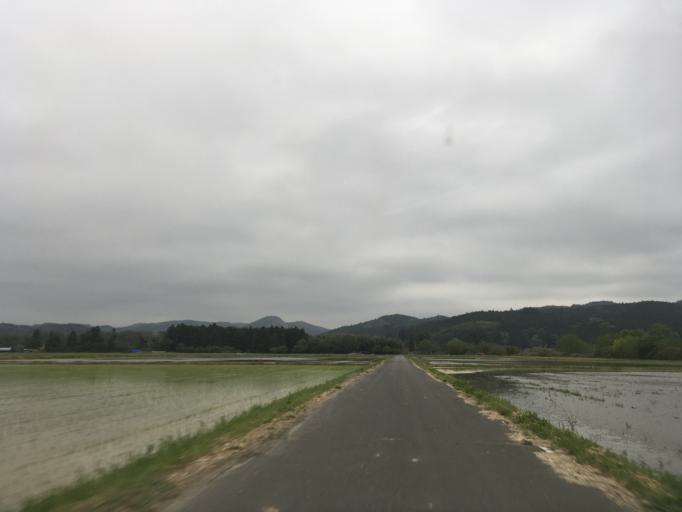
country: JP
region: Miyagi
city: Wakuya
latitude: 38.7145
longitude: 141.2882
